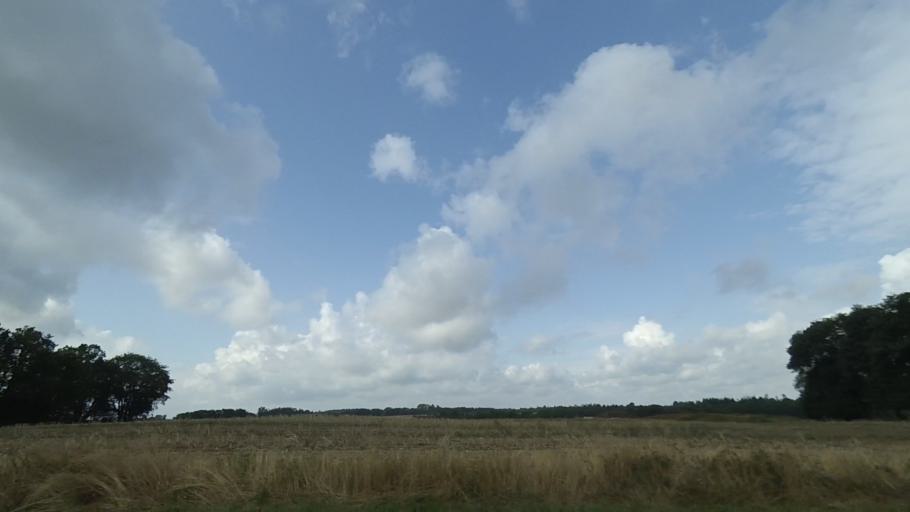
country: DK
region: Central Jutland
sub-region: Syddjurs Kommune
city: Ryomgard
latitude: 56.4203
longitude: 10.5575
